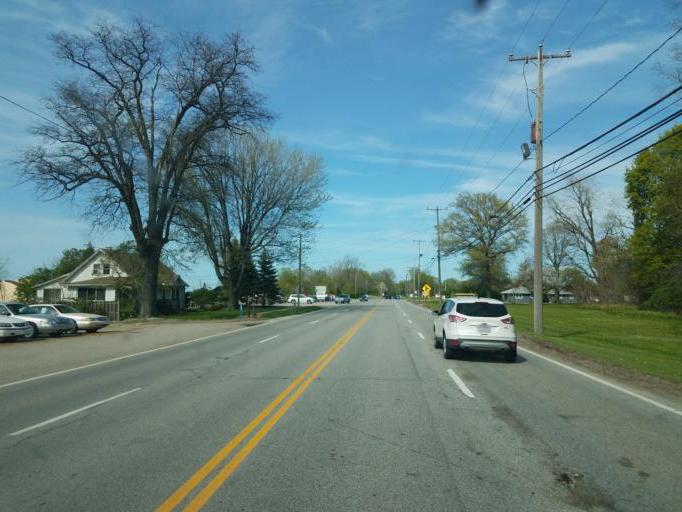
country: US
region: Ohio
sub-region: Lake County
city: Perry
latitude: 41.7599
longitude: -81.1909
